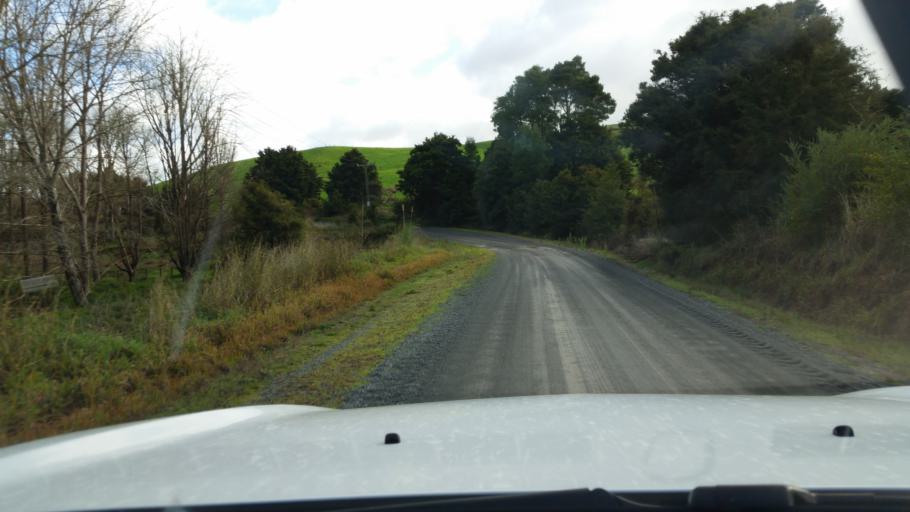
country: NZ
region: Northland
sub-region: Whangarei
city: Maungatapere
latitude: -35.6922
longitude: 174.1045
